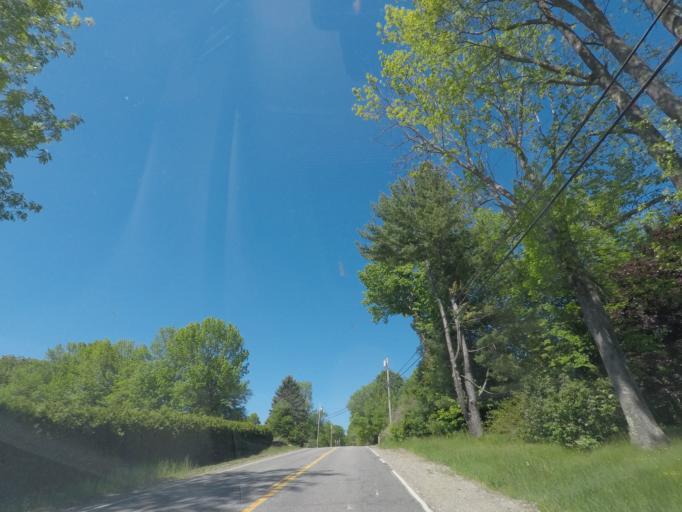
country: US
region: Maine
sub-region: Kennebec County
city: Gardiner
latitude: 44.2305
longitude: -69.8167
